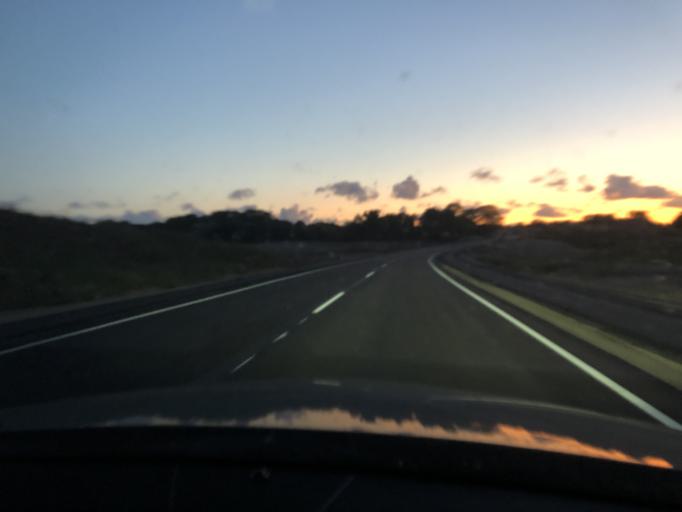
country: DK
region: Zealand
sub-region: Soro Kommune
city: Stenlille
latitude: 55.6584
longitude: 11.5716
